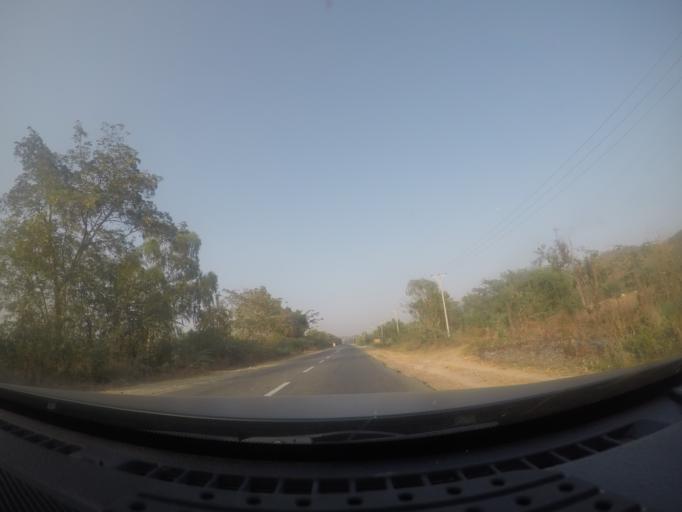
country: MM
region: Mandalay
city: Yamethin
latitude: 20.7198
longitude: 96.1914
